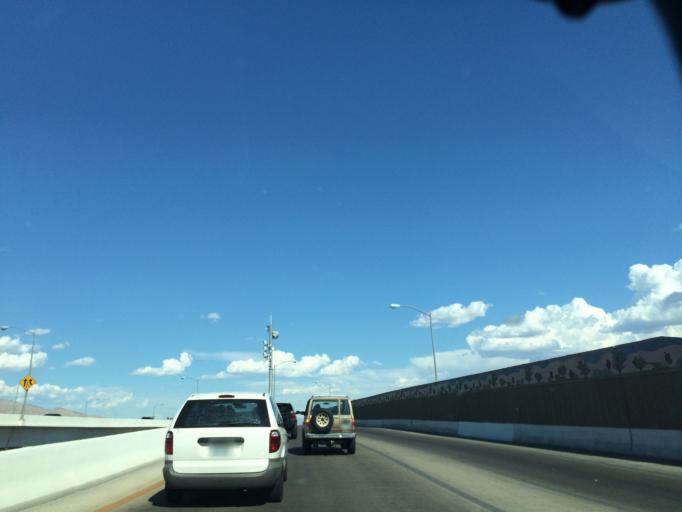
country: US
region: Nevada
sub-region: Clark County
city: Las Vegas
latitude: 36.1726
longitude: -115.1369
